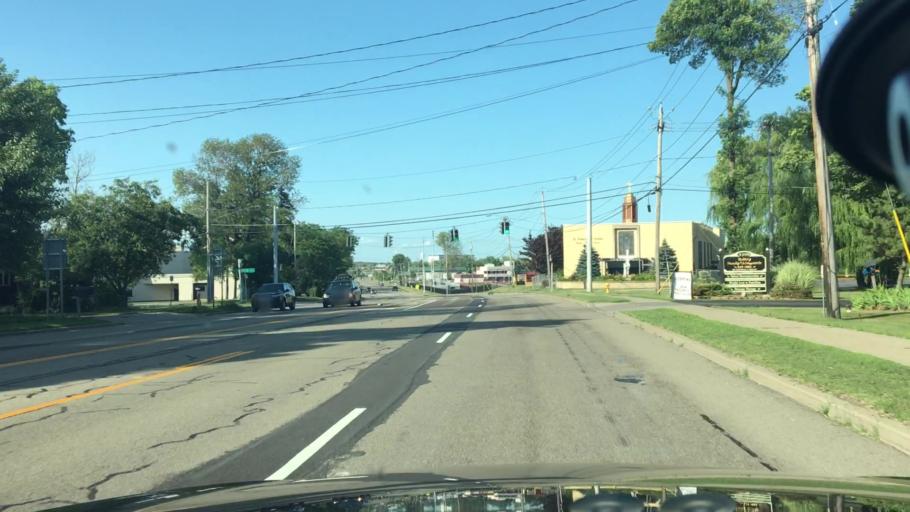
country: US
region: New York
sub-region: Erie County
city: Wanakah
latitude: 42.7680
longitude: -78.8645
